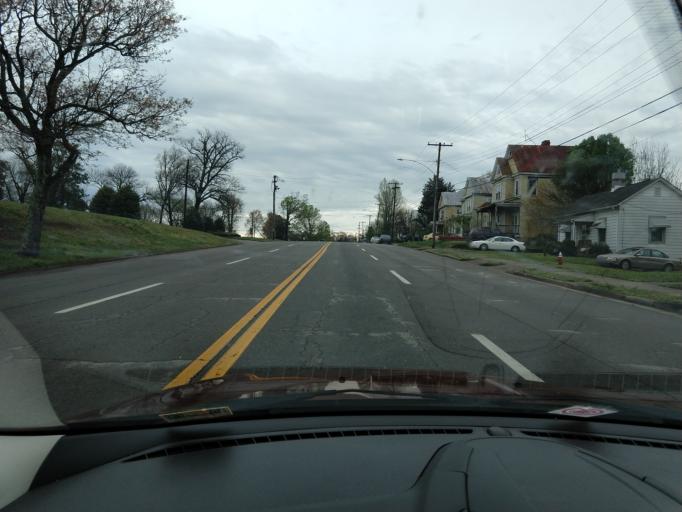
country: US
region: Virginia
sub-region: City of Danville
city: Danville
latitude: 36.5725
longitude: -79.4242
